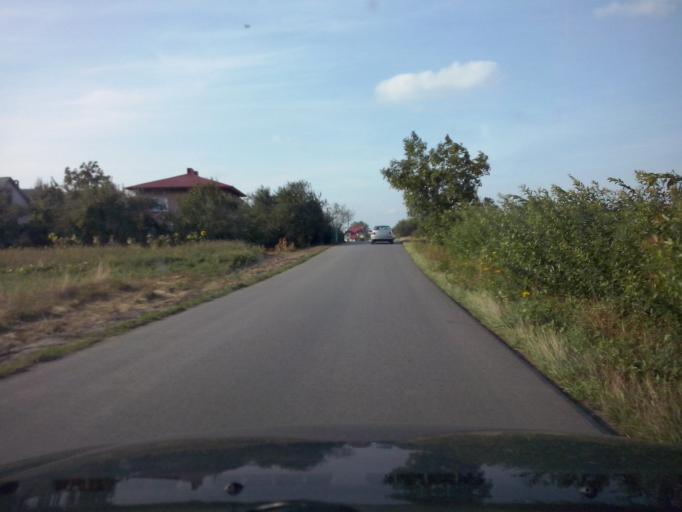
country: PL
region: Subcarpathian Voivodeship
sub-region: Powiat nizanski
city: Krzeszow
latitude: 50.3753
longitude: 22.3257
